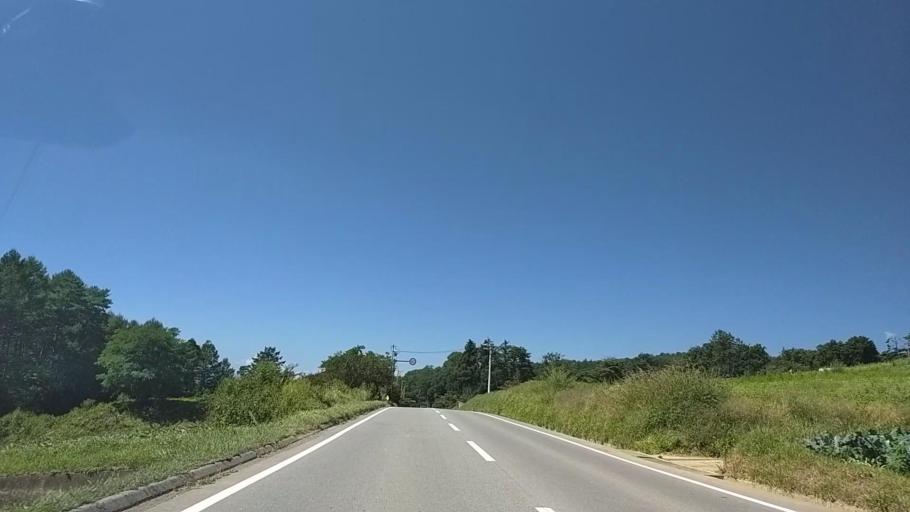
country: JP
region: Nagano
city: Komoro
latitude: 36.3432
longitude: 138.4877
